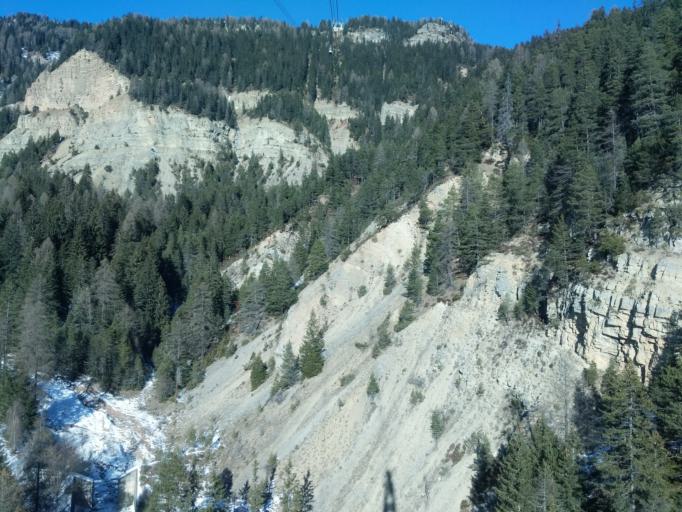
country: IT
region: Trentino-Alto Adige
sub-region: Provincia di Trento
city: Vigo di Fassa
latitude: 46.4250
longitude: 11.6695
